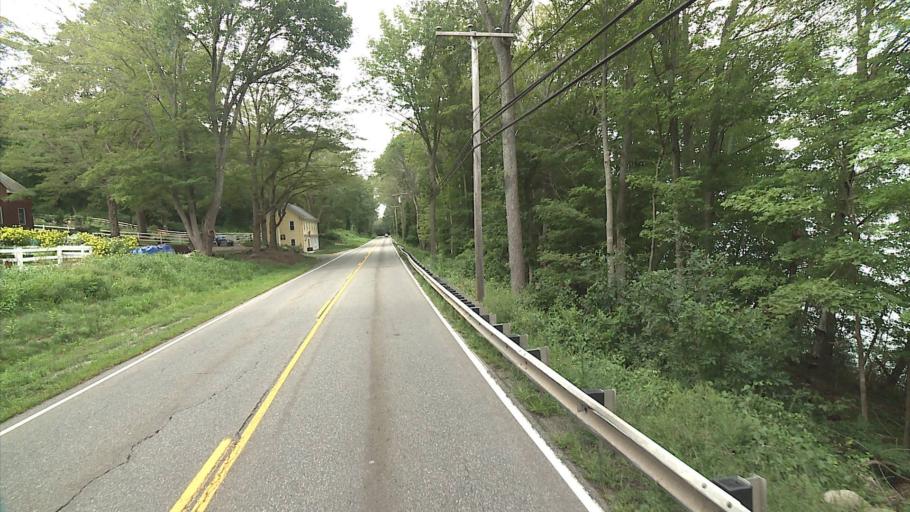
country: US
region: Connecticut
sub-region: New London County
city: Oxoboxo River
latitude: 41.4125
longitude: -72.1868
